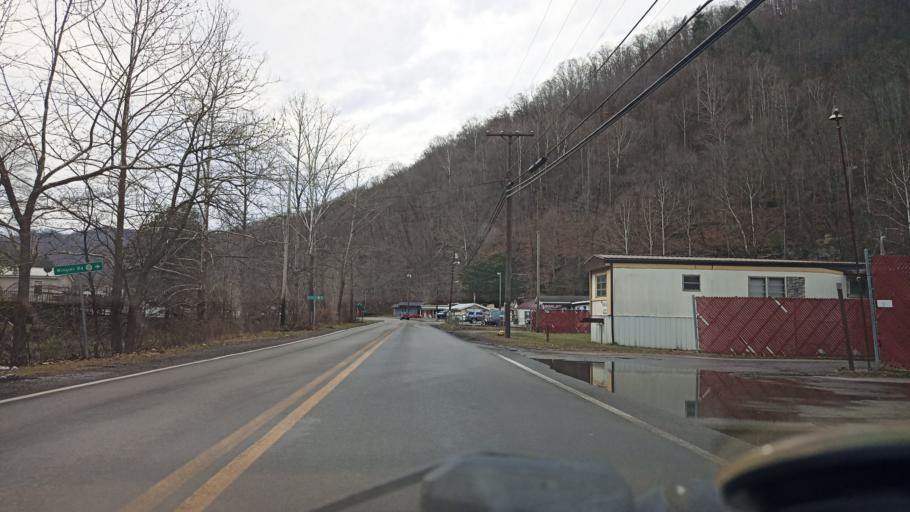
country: US
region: West Virginia
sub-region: Logan County
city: Mallory
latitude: 37.7569
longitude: -81.8579
